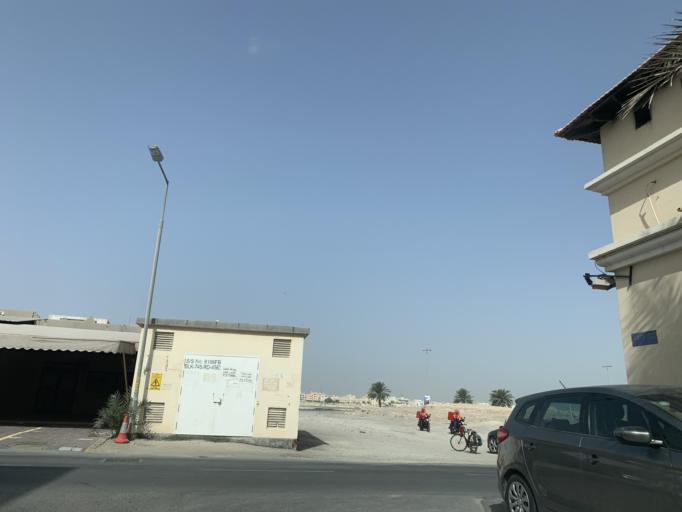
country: BH
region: Northern
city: Ar Rifa'
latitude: 26.1450
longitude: 50.5790
